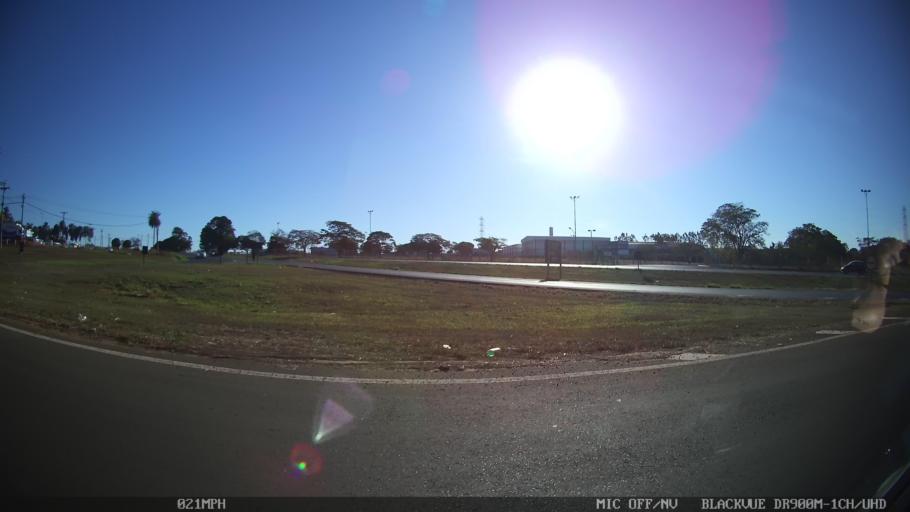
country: BR
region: Sao Paulo
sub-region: Olimpia
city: Olimpia
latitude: -20.6909
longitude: -48.9175
